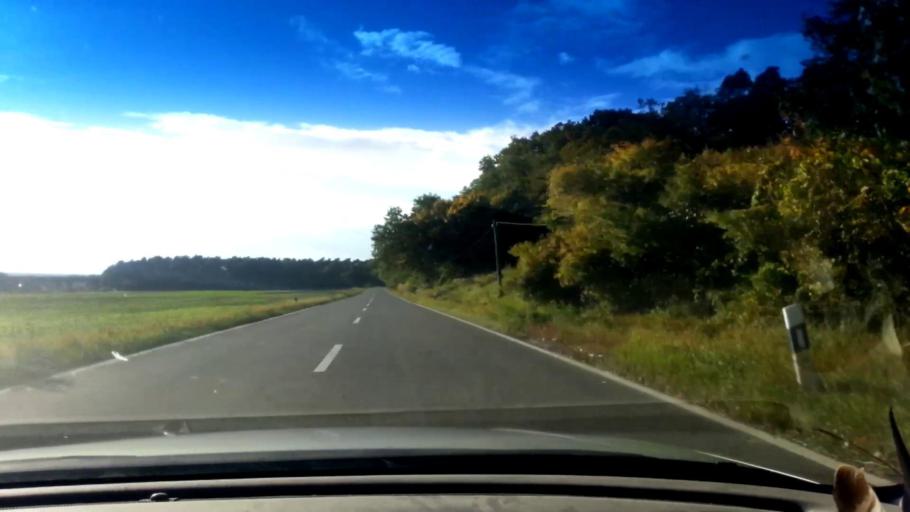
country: DE
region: Bavaria
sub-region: Upper Franconia
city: Strullendorf
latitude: 49.8567
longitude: 10.9897
